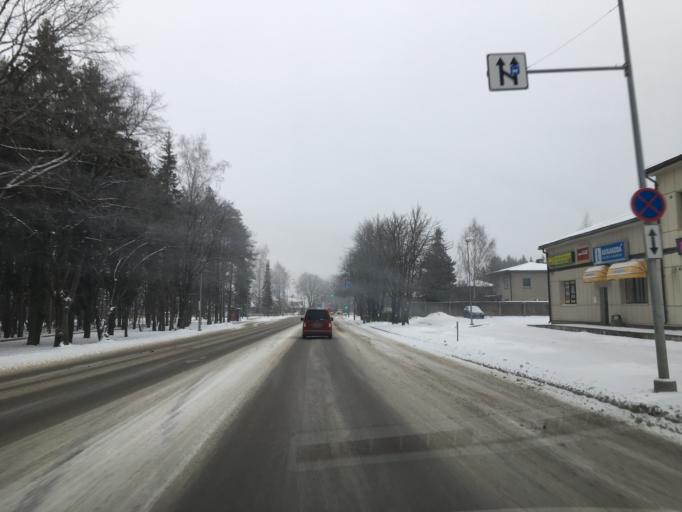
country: EE
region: Tartu
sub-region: Tartu linn
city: Tartu
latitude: 58.3606
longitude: 26.6888
